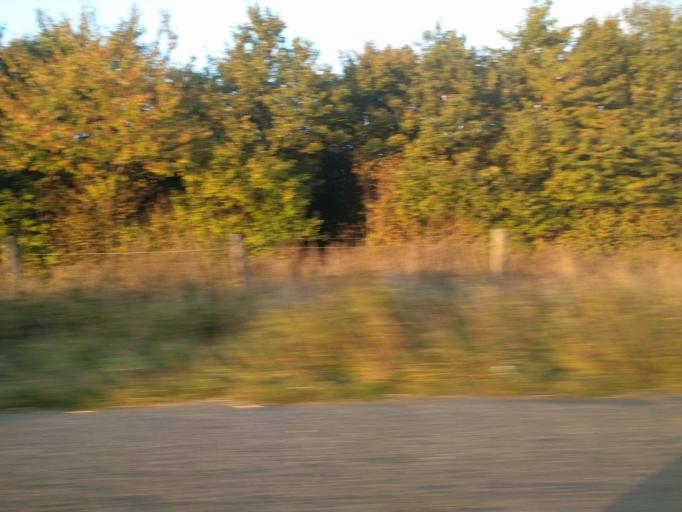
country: DK
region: South Denmark
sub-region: Nyborg Kommune
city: Ullerslev
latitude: 55.3379
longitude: 10.7201
